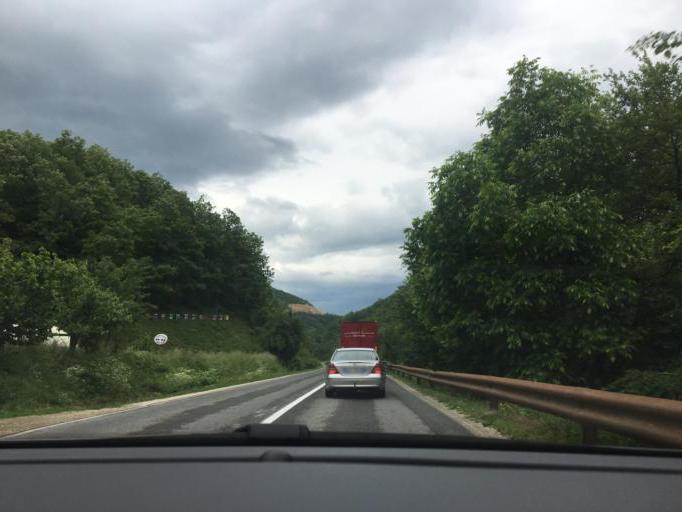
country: MK
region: Drugovo
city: Drugovo
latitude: 41.4794
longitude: 20.8857
